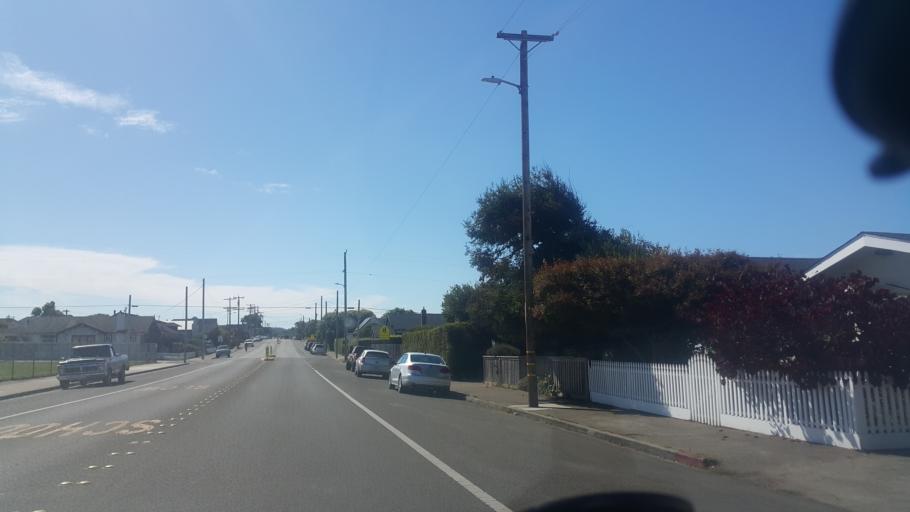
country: US
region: California
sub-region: Mendocino County
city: Fort Bragg
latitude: 39.4463
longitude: -123.7981
